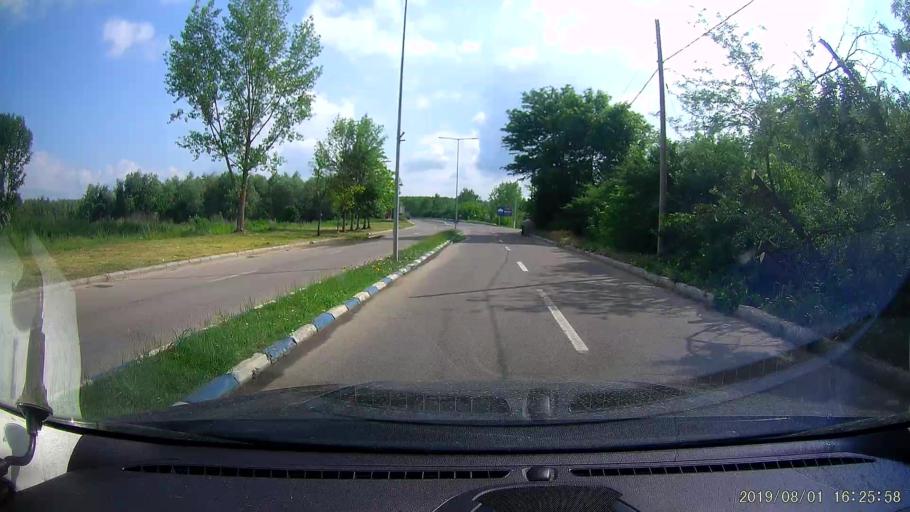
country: RO
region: Calarasi
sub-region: Municipiul Calarasi
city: Calarasi
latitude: 44.1881
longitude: 27.3228
